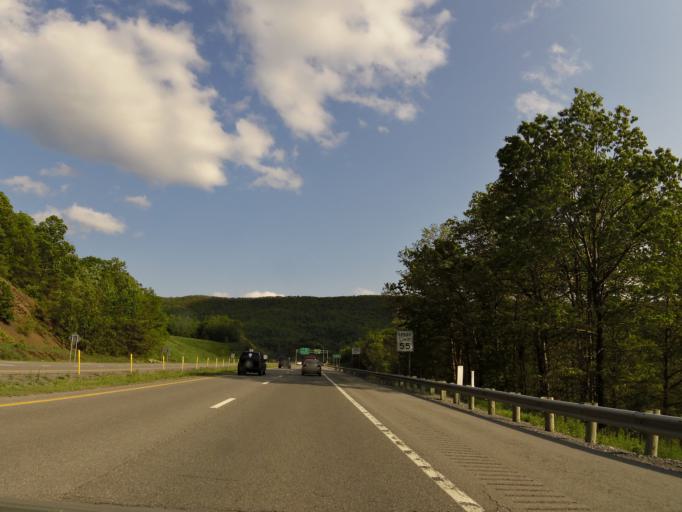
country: US
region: West Virginia
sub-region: Mercer County
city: Bluefield
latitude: 37.2818
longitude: -81.1671
